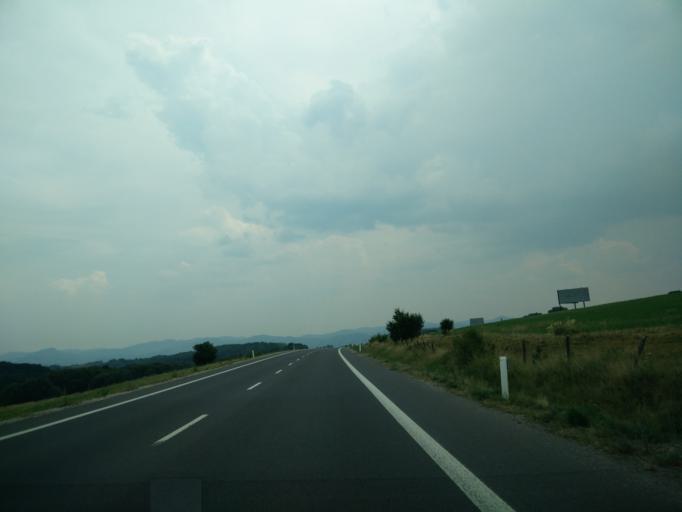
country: SK
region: Banskobystricky
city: Ziar nad Hronom
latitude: 48.6372
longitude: 18.7747
